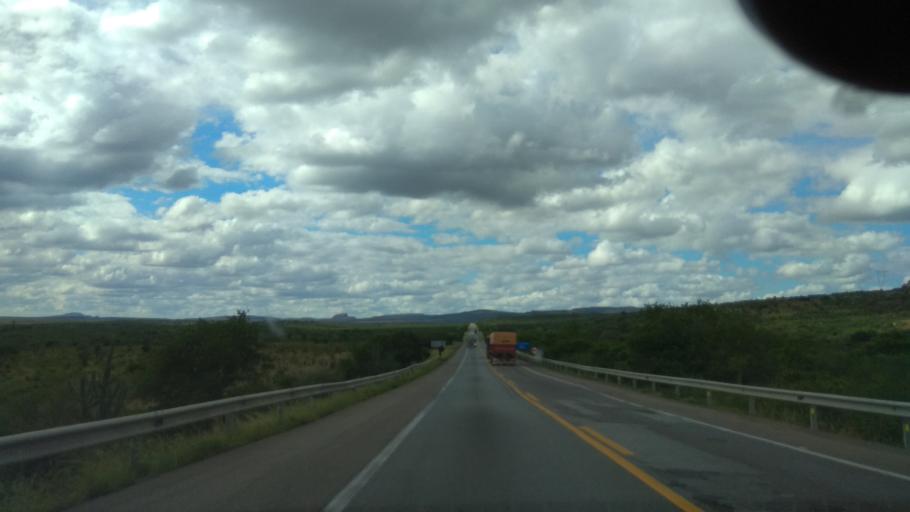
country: BR
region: Bahia
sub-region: Amargosa
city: Amargosa
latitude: -12.9567
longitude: -39.9224
